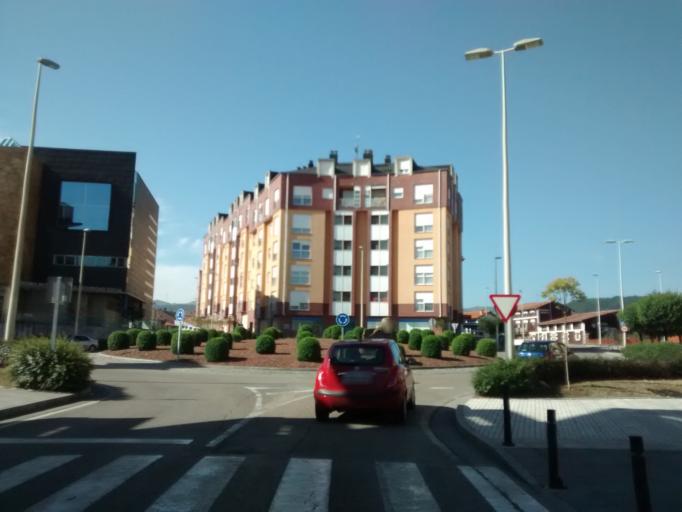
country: ES
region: Cantabria
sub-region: Provincia de Cantabria
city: Torrelavega
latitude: 43.3454
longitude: -4.0567
